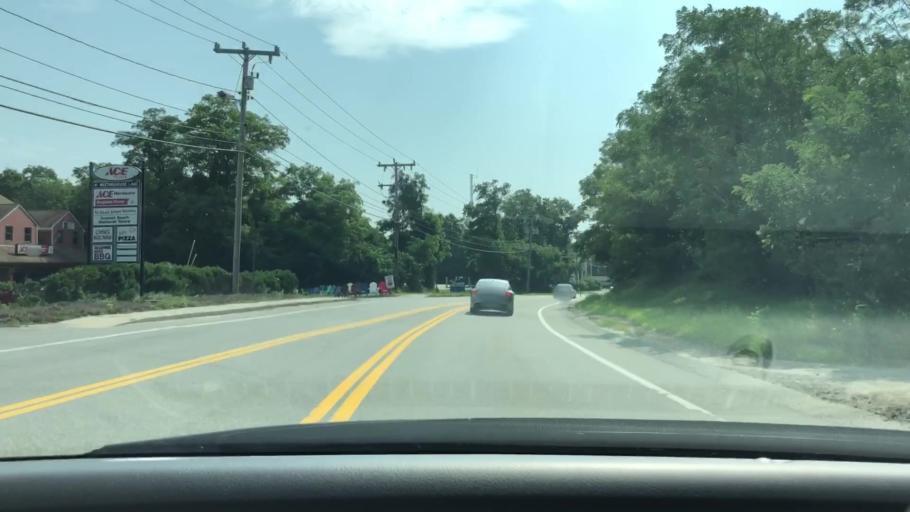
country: US
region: Massachusetts
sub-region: Barnstable County
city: Sagamore
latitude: 41.7819
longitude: -70.5391
